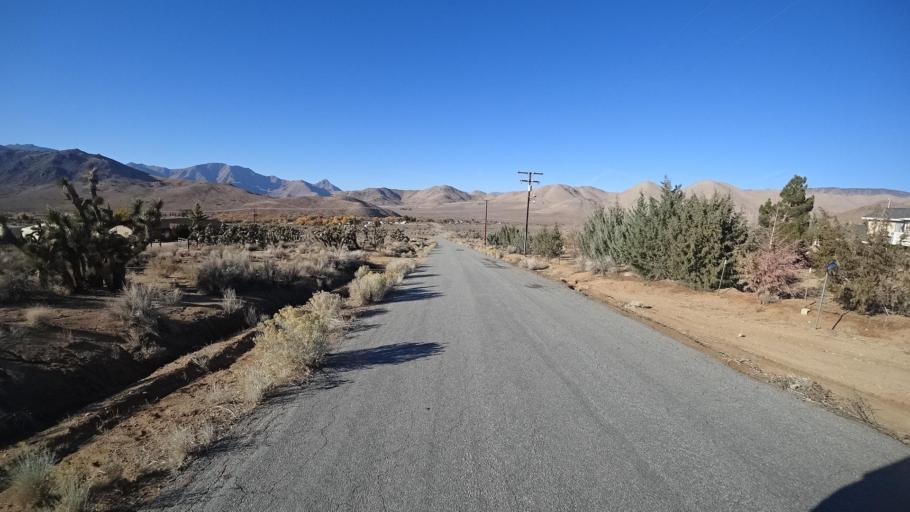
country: US
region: California
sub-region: Kern County
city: Weldon
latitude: 35.5349
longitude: -118.2024
